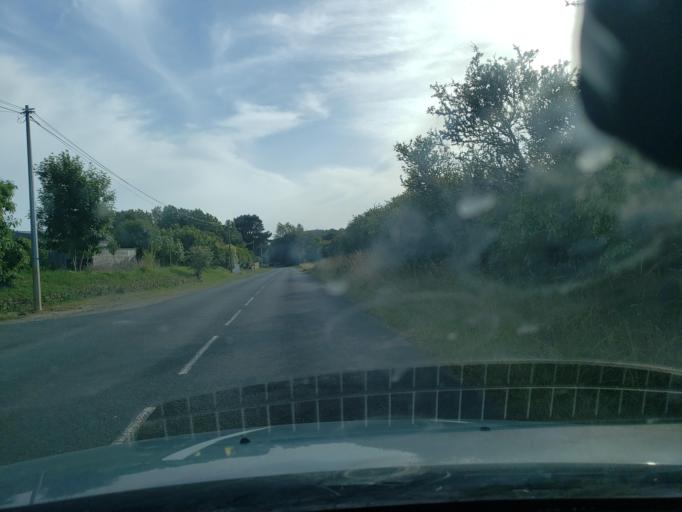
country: FR
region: Brittany
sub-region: Departement du Finistere
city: Treffiagat
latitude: 47.8132
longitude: -4.2445
